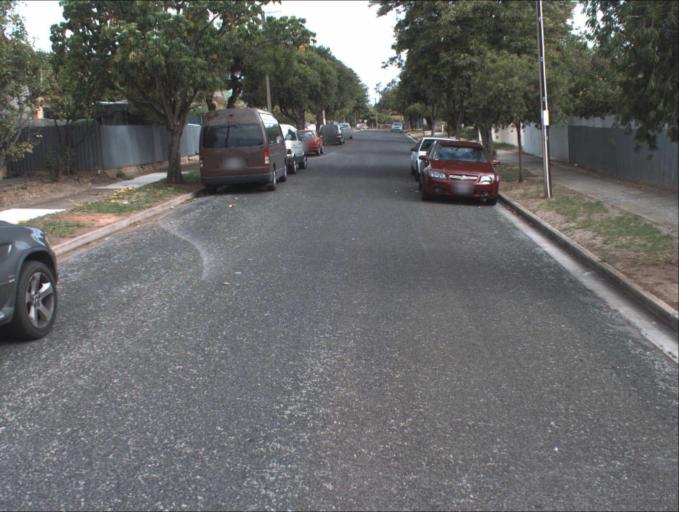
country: AU
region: South Australia
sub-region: Port Adelaide Enfield
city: Blair Athol
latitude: -34.8639
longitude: 138.5960
